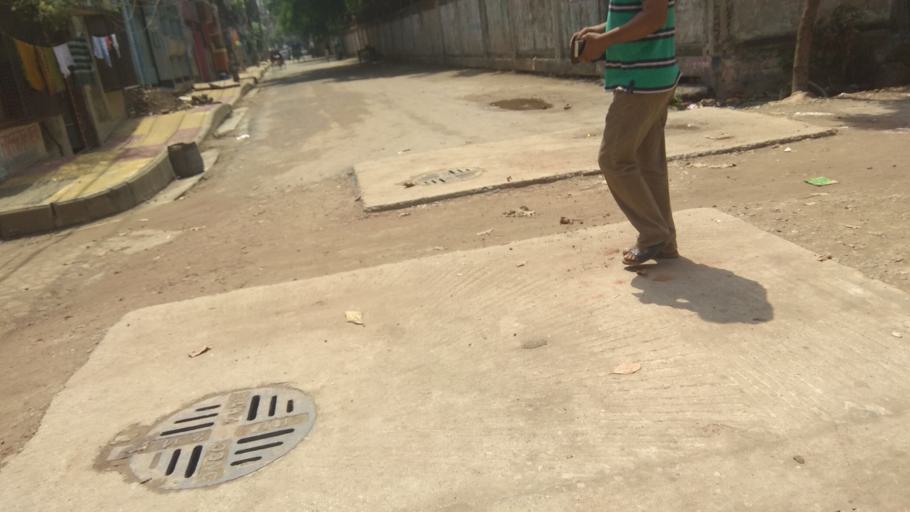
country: BD
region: Dhaka
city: Tungi
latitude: 23.8156
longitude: 90.3538
